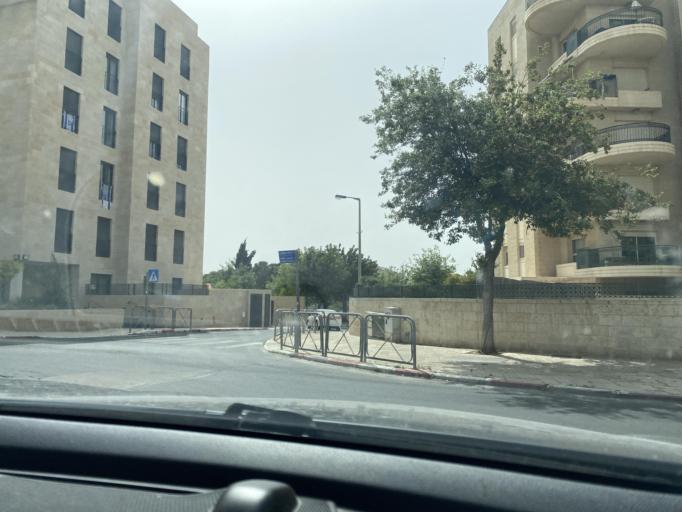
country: IL
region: Jerusalem
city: Jerusalem
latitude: 31.7574
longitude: 35.2253
